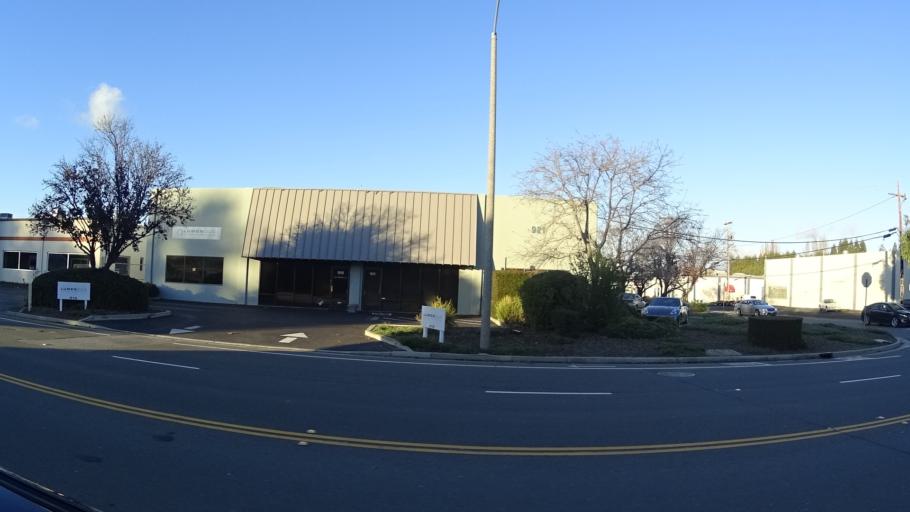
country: US
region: California
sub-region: Santa Clara County
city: Sunnyvale
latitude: 37.3743
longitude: -122.0093
